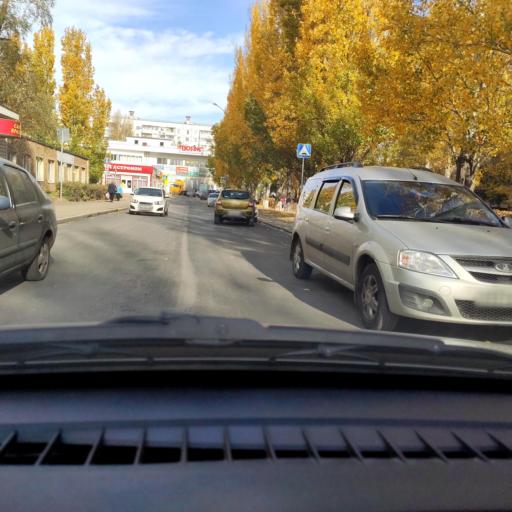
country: RU
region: Samara
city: Tol'yatti
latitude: 53.5202
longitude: 49.3034
